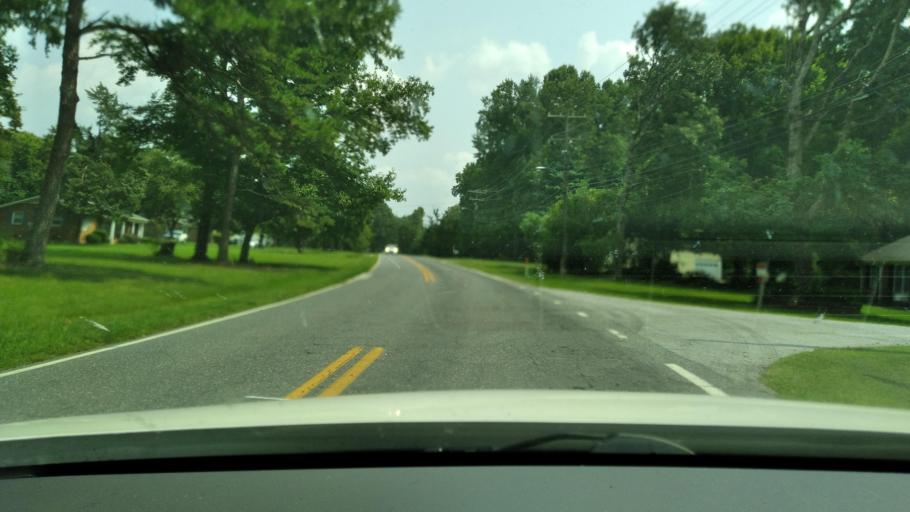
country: US
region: North Carolina
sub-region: Guilford County
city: Jamestown
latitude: 36.0414
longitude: -79.8906
